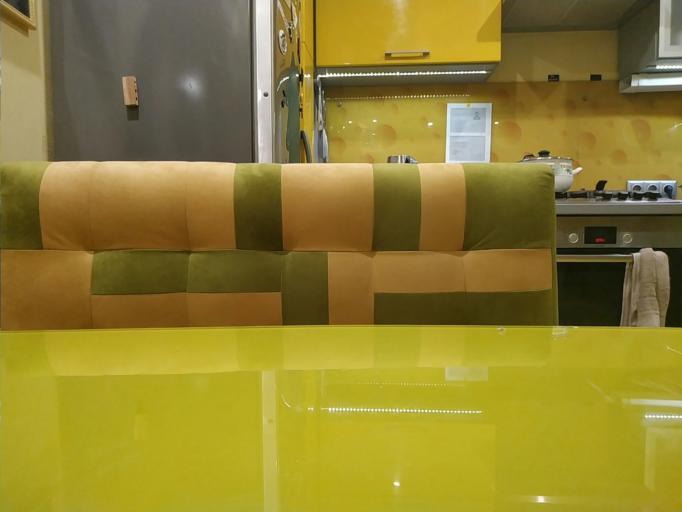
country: RU
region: Murmansk
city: Alakurtti
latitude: 66.2202
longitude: 30.2810
